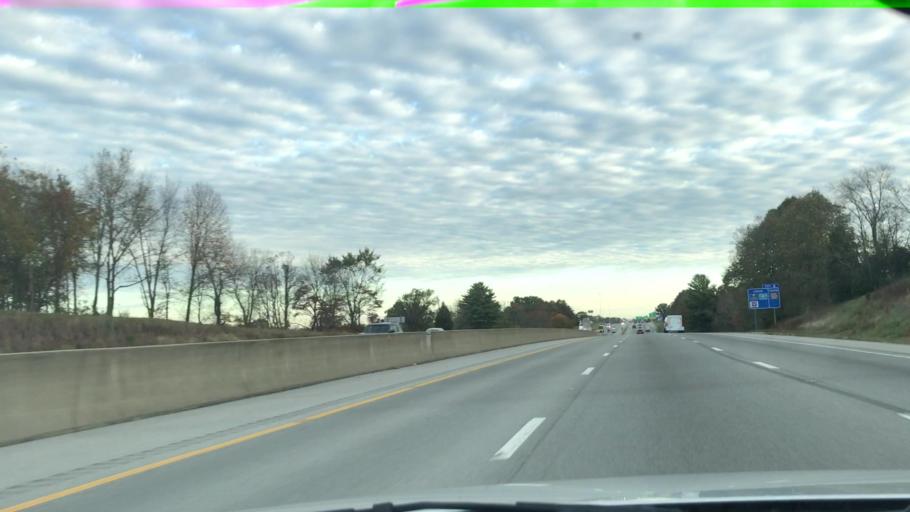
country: US
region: Kentucky
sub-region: Simpson County
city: Franklin
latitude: 36.7029
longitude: -86.5289
